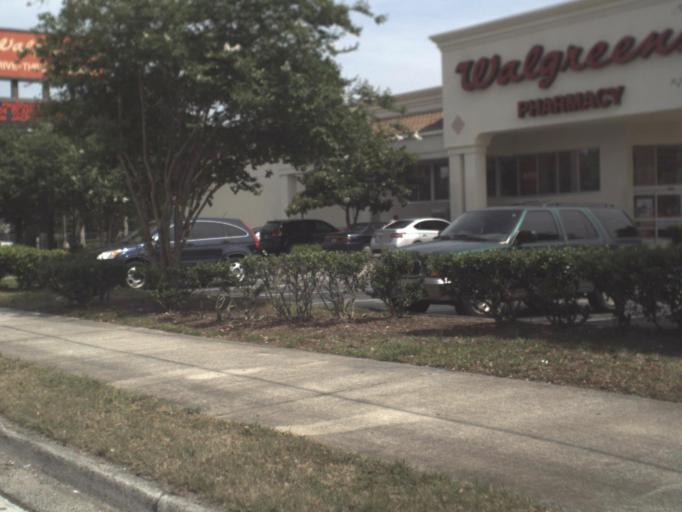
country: US
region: Florida
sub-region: Clay County
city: Bellair-Meadowbrook Terrace
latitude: 30.2481
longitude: -81.7729
